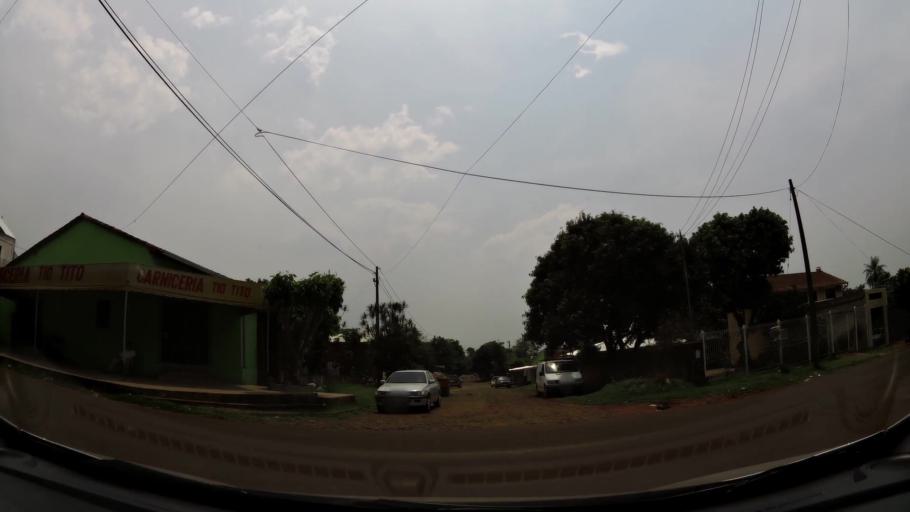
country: BR
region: Parana
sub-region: Foz Do Iguacu
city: Foz do Iguacu
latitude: -25.5655
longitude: -54.6119
